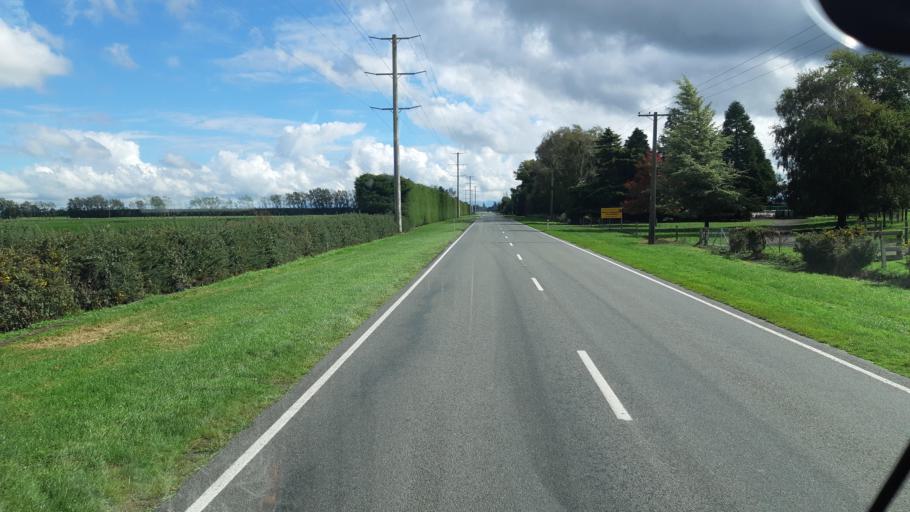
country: NZ
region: Canterbury
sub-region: Selwyn District
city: Darfield
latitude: -43.4747
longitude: 172.2655
